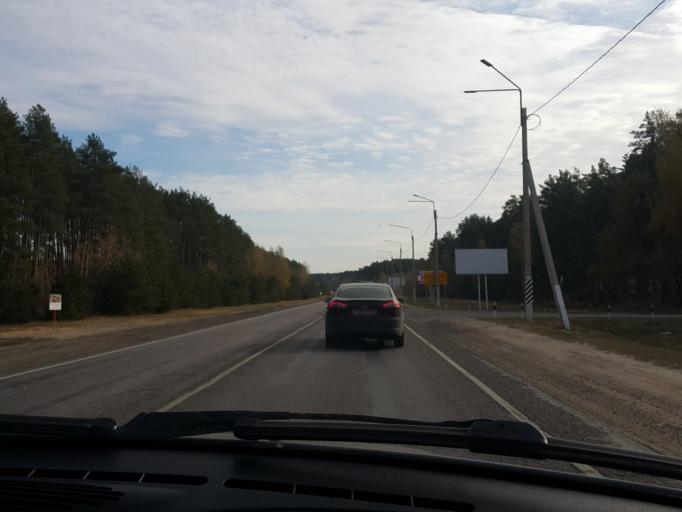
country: RU
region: Tambov
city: Donskoye
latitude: 52.7124
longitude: 41.5218
